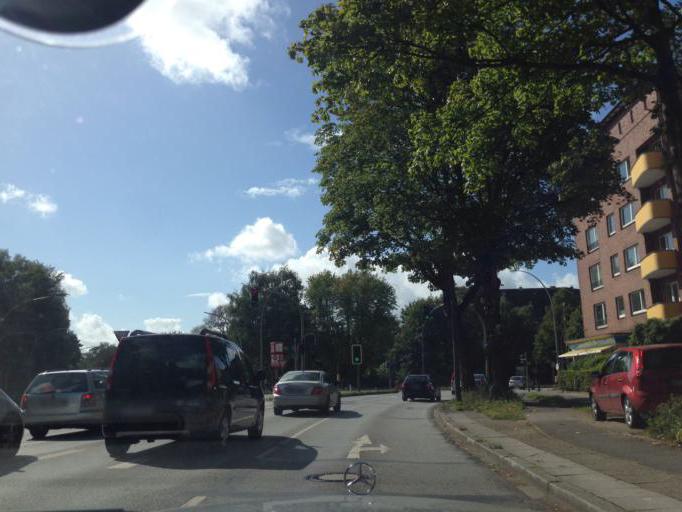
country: DE
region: Hamburg
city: Winterhude
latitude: 53.5996
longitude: 10.0075
